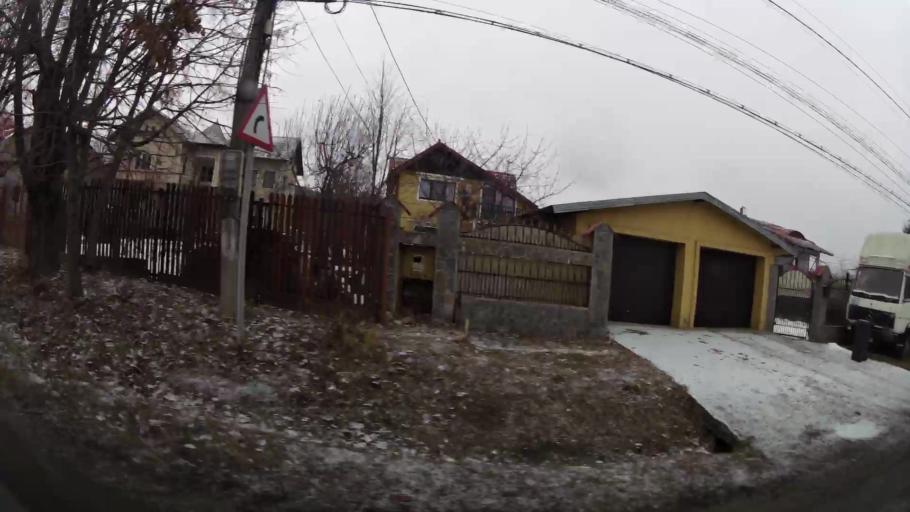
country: RO
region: Dambovita
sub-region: Municipiul Targoviste
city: Targoviste
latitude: 44.9402
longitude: 25.4913
